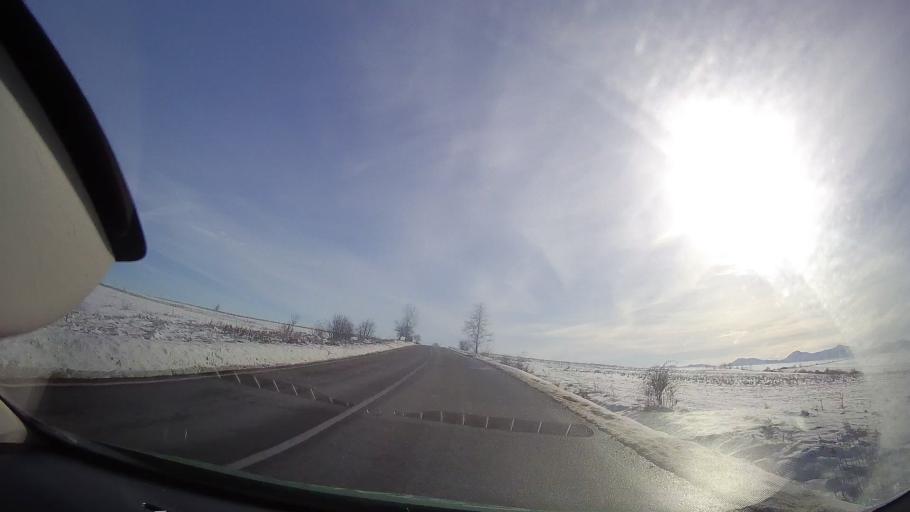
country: RO
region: Neamt
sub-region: Comuna Baltatesti
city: Valea Seaca
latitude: 47.1619
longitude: 26.3183
